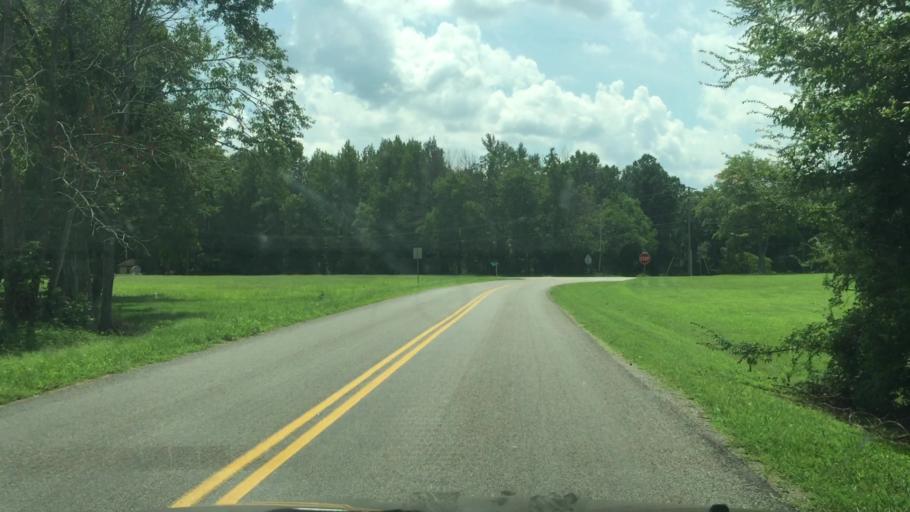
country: US
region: Virginia
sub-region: Hanover County
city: Ashland
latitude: 37.7489
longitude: -77.4988
